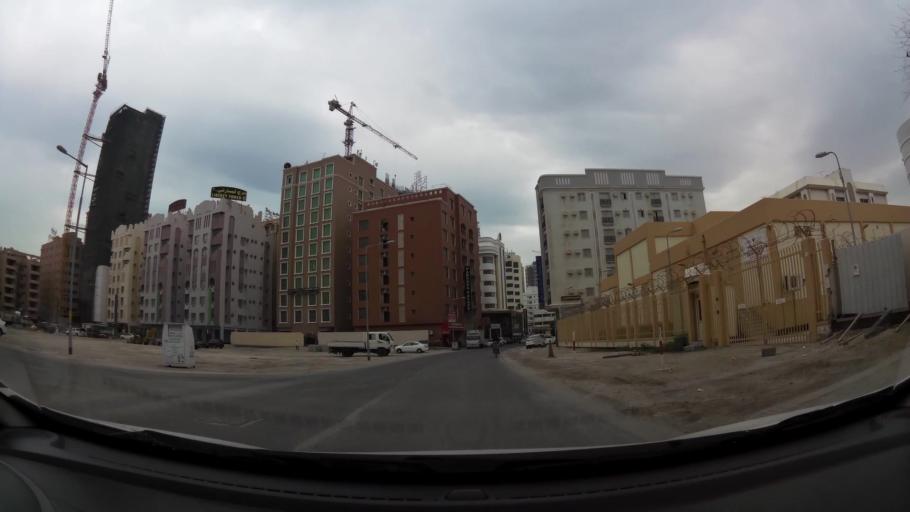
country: BH
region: Manama
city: Manama
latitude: 26.2355
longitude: 50.5952
